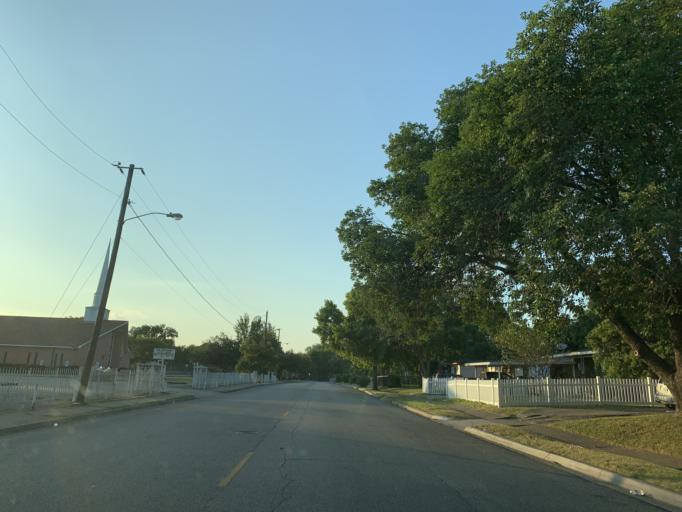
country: US
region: Texas
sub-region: Dallas County
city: Hutchins
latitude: 32.6982
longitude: -96.7690
